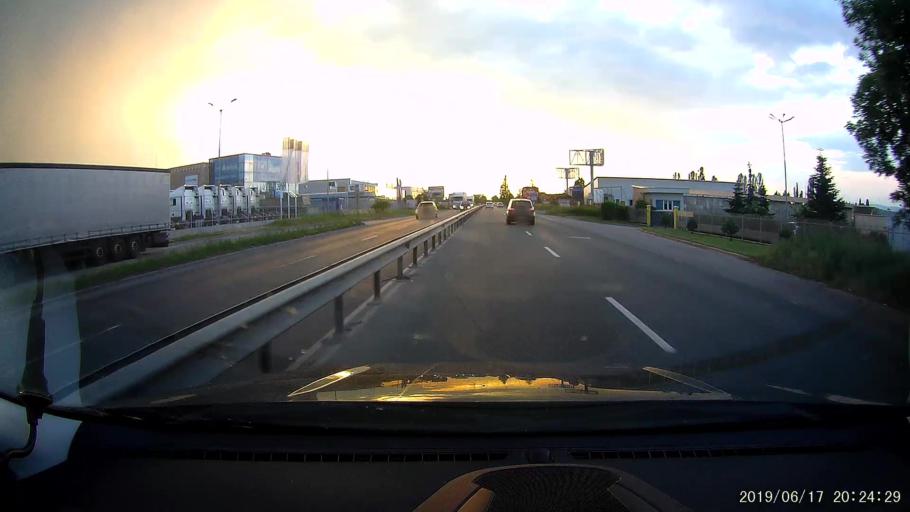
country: BG
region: Sofiya
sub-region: Obshtina Bozhurishte
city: Bozhurishte
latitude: 42.7413
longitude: 23.2360
